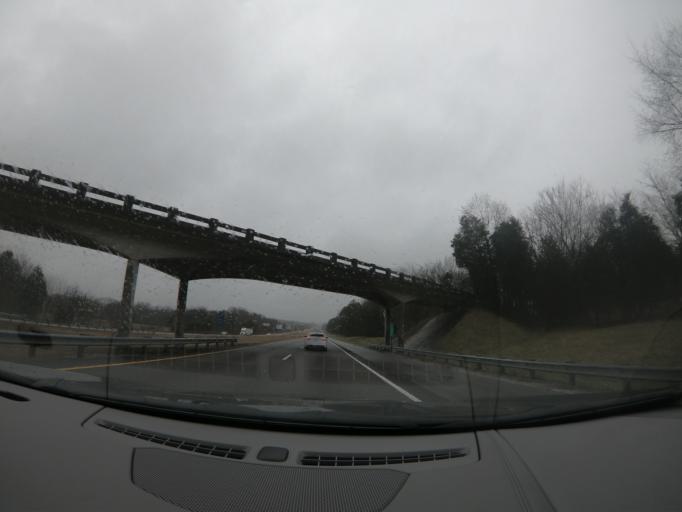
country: US
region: Tennessee
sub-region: Franklin County
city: Sewanee
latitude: 35.3637
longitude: -85.9625
